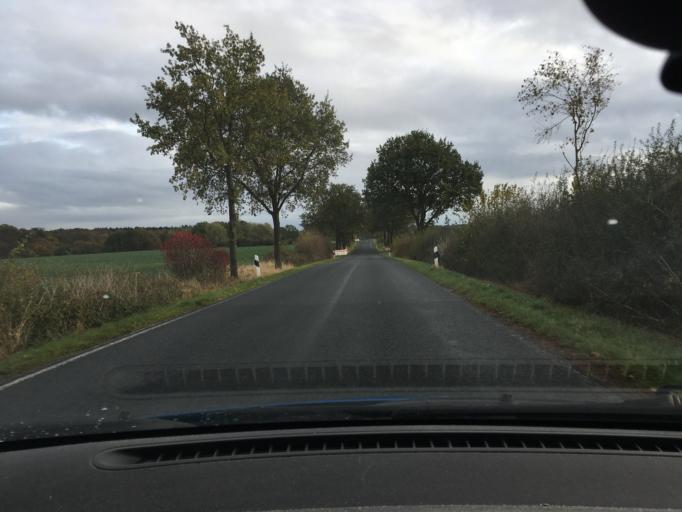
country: DE
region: Schleswig-Holstein
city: Lankau
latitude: 53.6566
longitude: 10.6887
